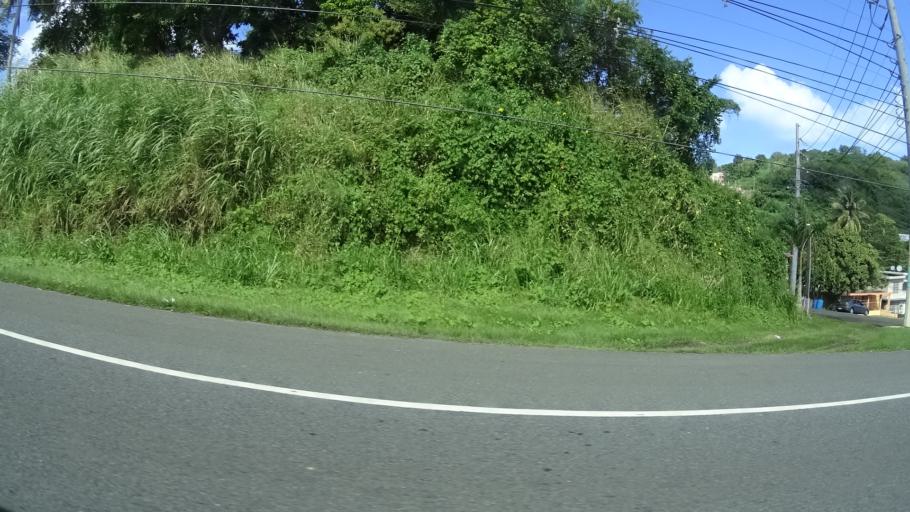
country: PR
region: Rio Grande
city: Palmer
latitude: 18.3706
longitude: -65.7759
